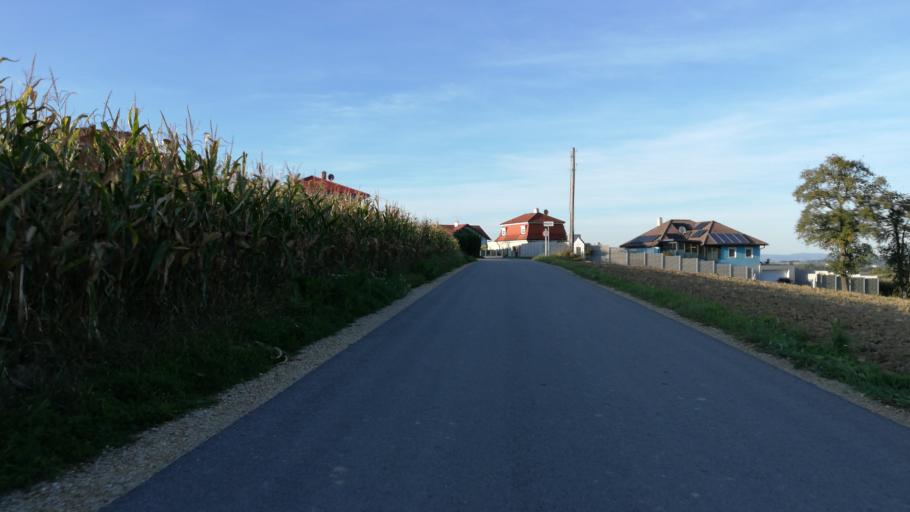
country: AT
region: Upper Austria
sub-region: Politischer Bezirk Grieskirchen
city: Bad Schallerbach
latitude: 48.1759
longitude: 13.8936
